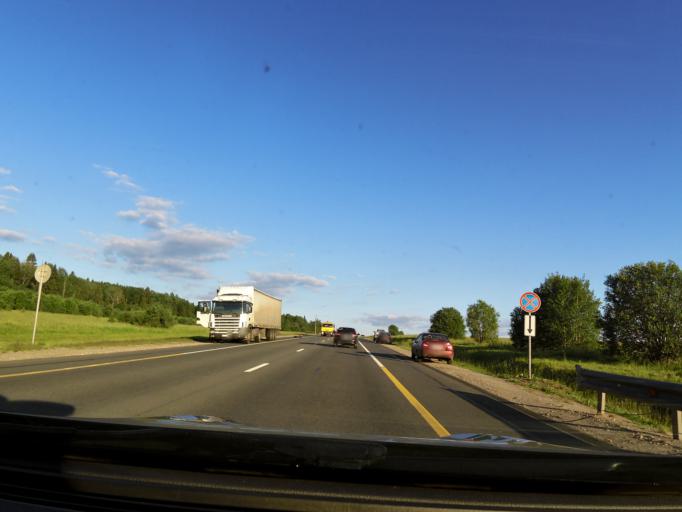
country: RU
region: Vologda
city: Vologda
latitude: 59.1139
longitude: 39.9774
